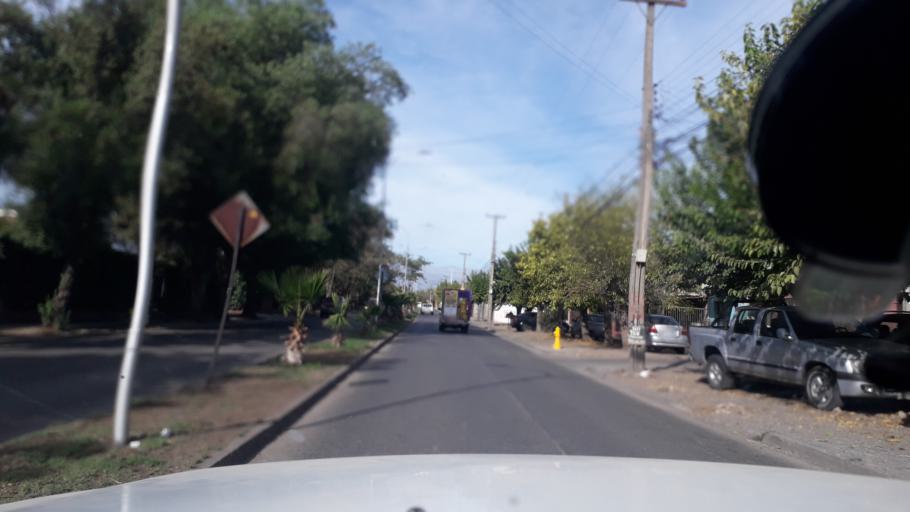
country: CL
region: Valparaiso
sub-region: Provincia de San Felipe
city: San Felipe
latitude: -32.7493
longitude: -70.7134
